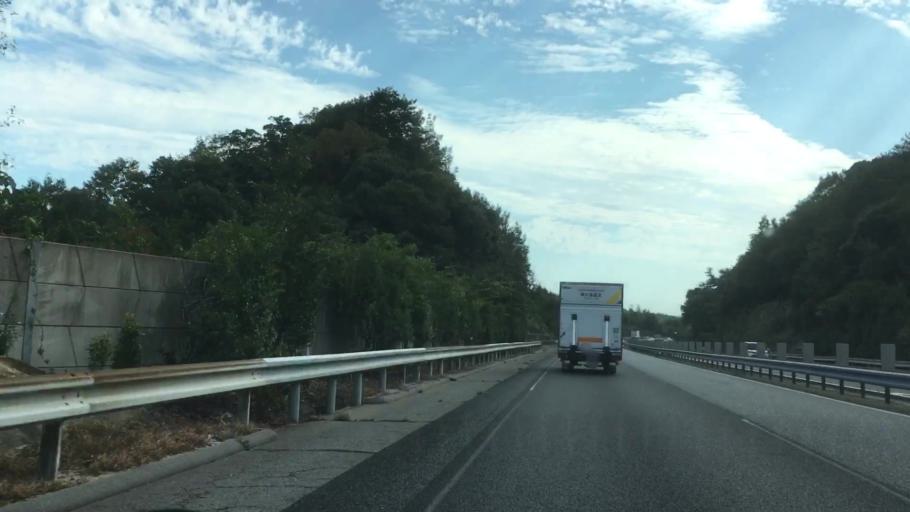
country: JP
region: Hiroshima
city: Ono-hara
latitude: 34.3109
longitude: 132.2803
